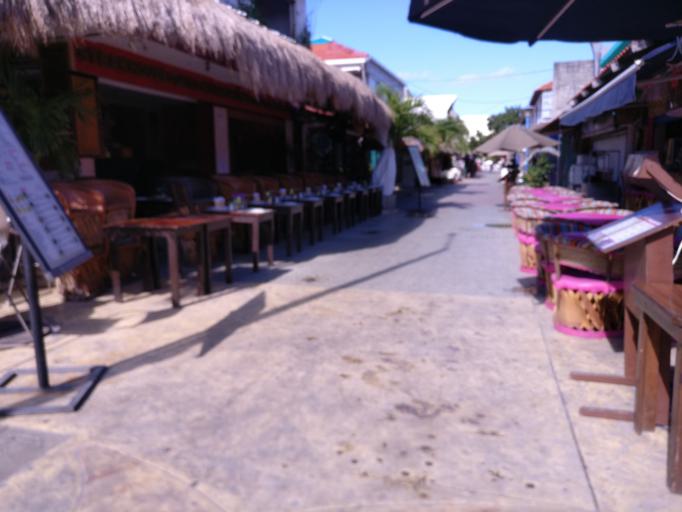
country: MX
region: Quintana Roo
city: Isla Mujeres
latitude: 21.2577
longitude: -86.7485
